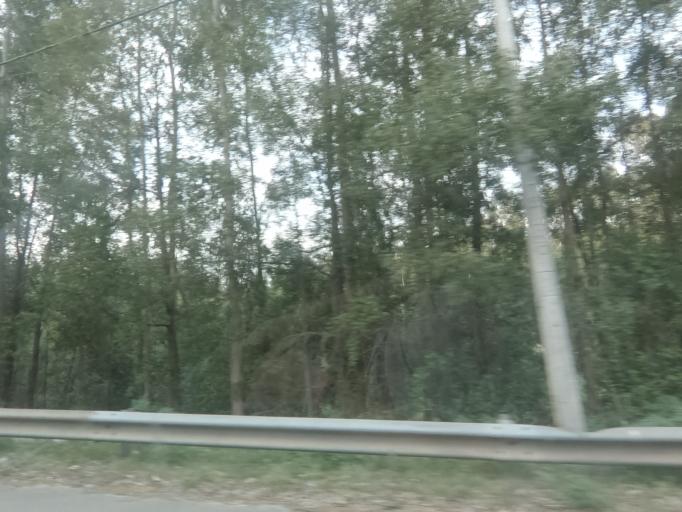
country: PT
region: Porto
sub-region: Valongo
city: Valongo
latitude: 41.1966
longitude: -8.5209
